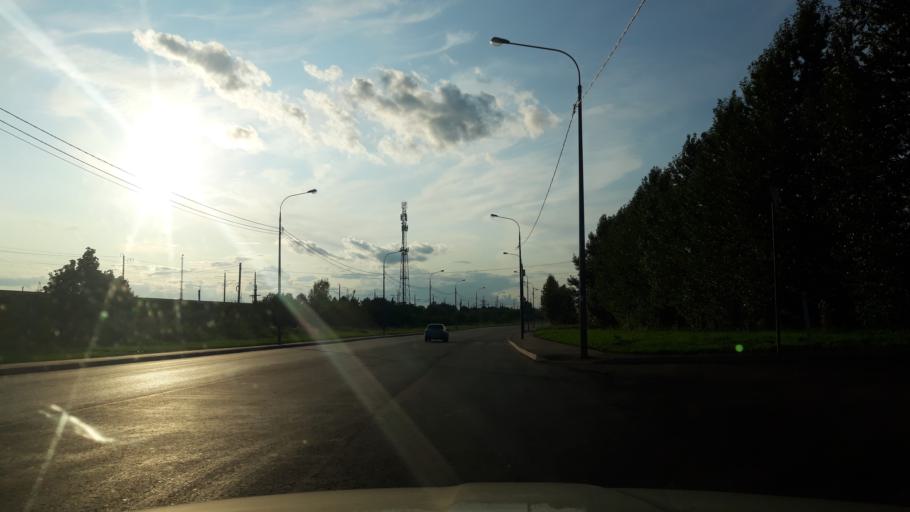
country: RU
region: Moskovskaya
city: Alabushevo
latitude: 56.0034
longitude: 37.1487
